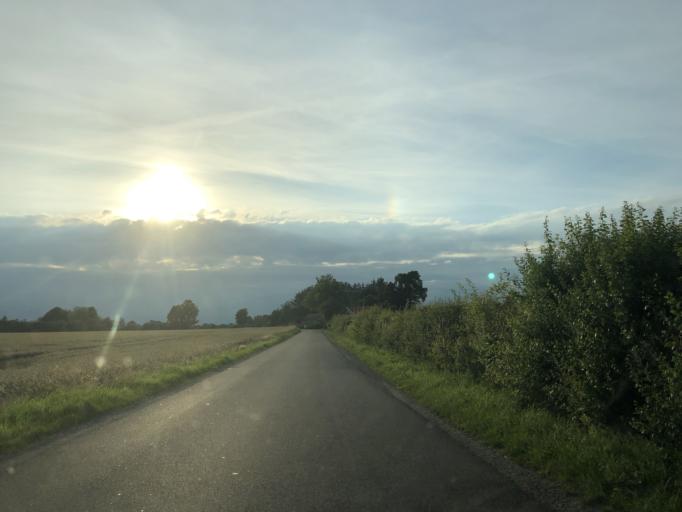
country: DK
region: South Denmark
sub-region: Vejle Kommune
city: Borkop
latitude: 55.6160
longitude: 9.6076
